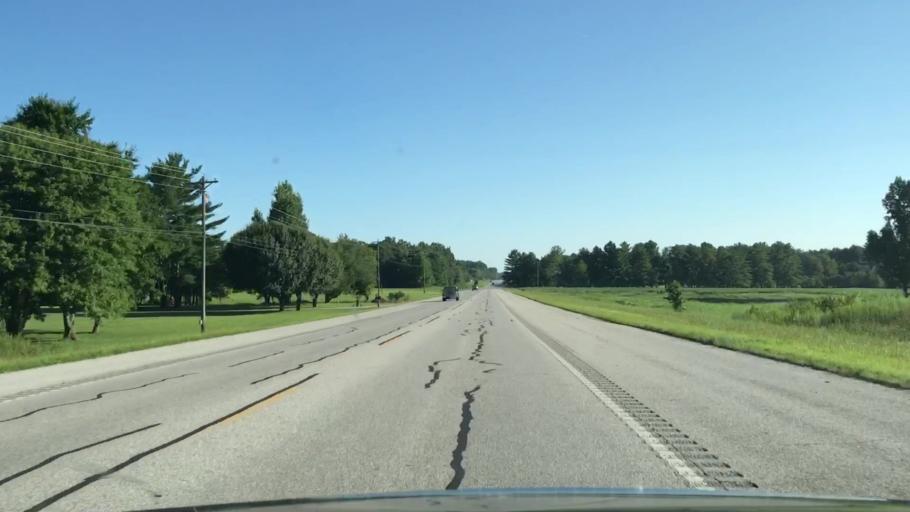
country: US
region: Tennessee
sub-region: Putnam County
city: Baxter
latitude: 36.1854
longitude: -85.6220
